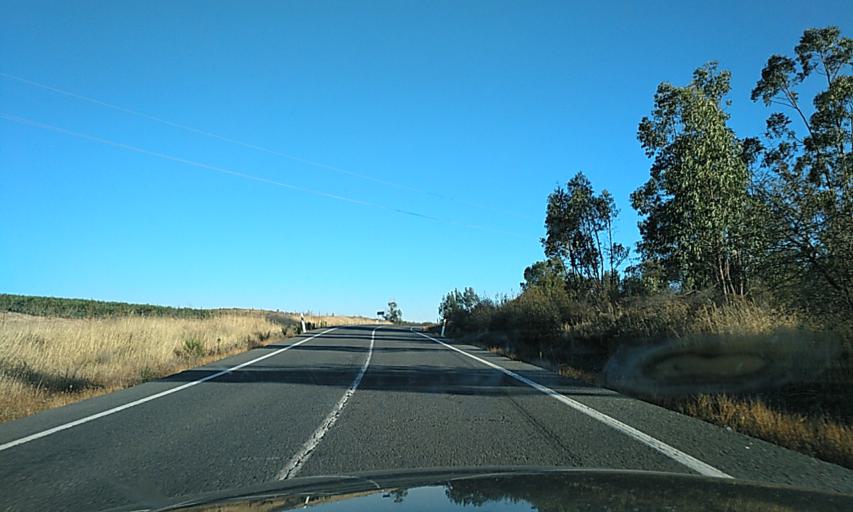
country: ES
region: Andalusia
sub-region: Provincia de Huelva
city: San Bartolome de la Torre
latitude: 37.4892
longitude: -7.1325
